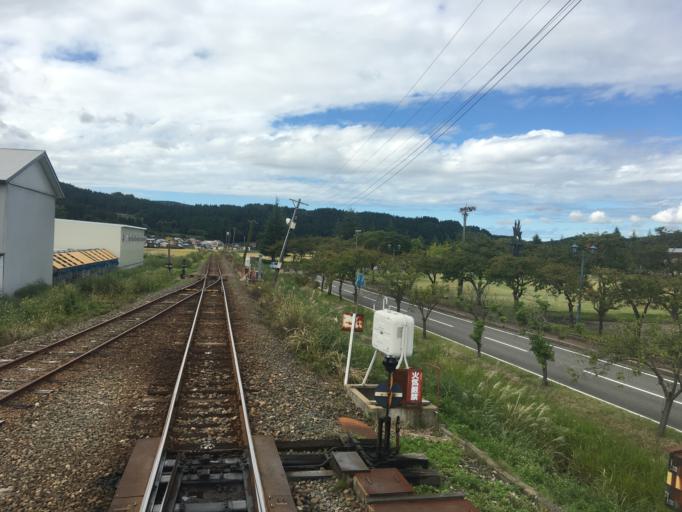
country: JP
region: Yamagata
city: Yuza
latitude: 39.2311
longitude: 140.1381
